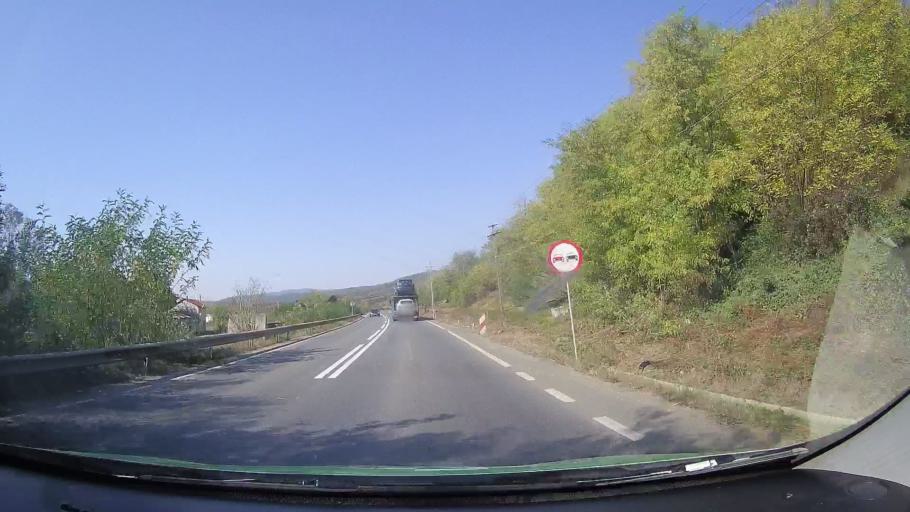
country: RO
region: Arad
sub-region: Comuna Conop
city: Conop
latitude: 46.1042
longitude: 21.8707
